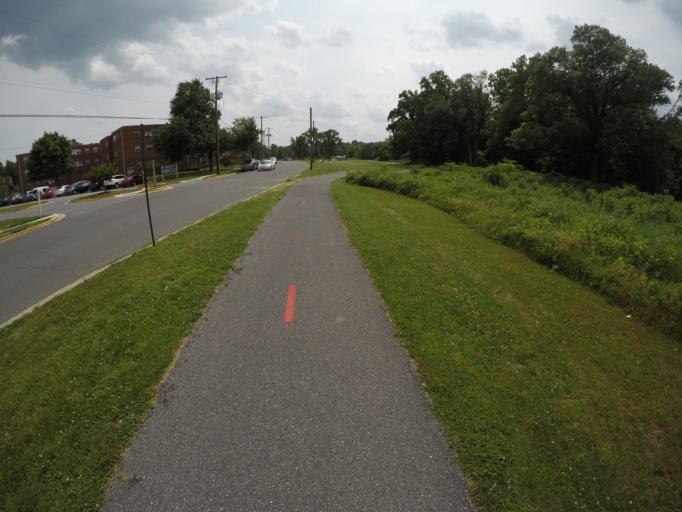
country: US
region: Maryland
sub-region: Prince George's County
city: Chillum
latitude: 38.9601
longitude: -76.9721
